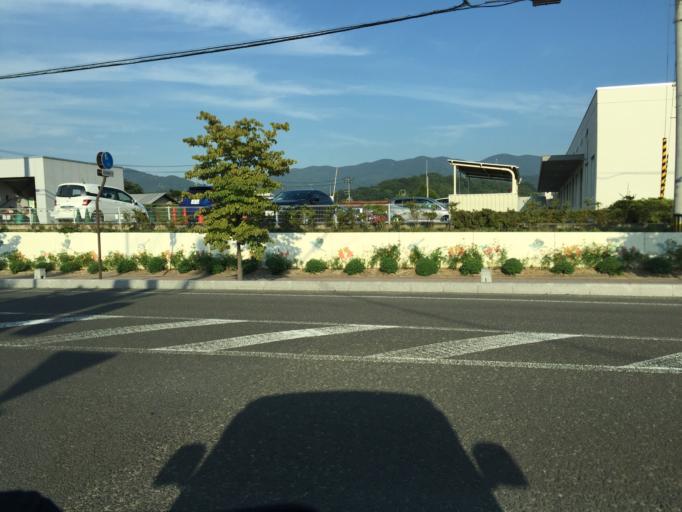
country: JP
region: Fukushima
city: Fukushima-shi
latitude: 37.6644
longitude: 140.5955
